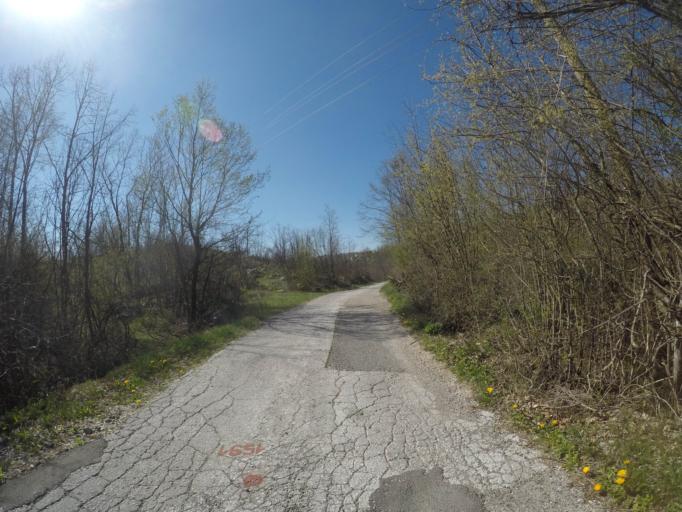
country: ME
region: Danilovgrad
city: Danilovgrad
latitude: 42.5403
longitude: 19.0104
